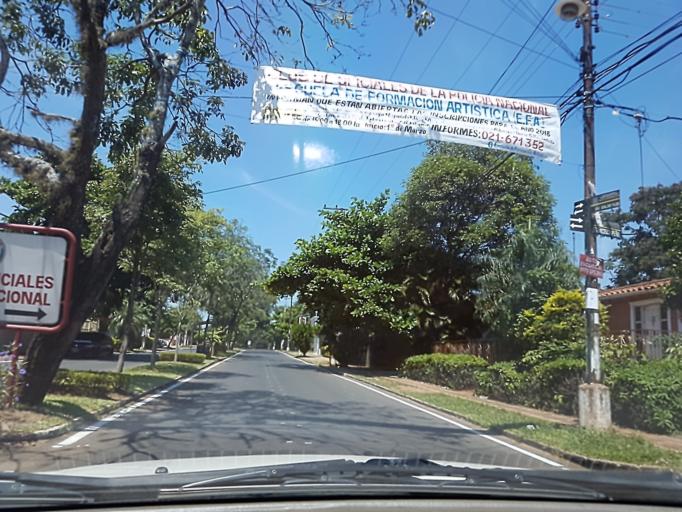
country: PY
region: Central
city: Fernando de la Mora
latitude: -25.2873
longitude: -57.5247
